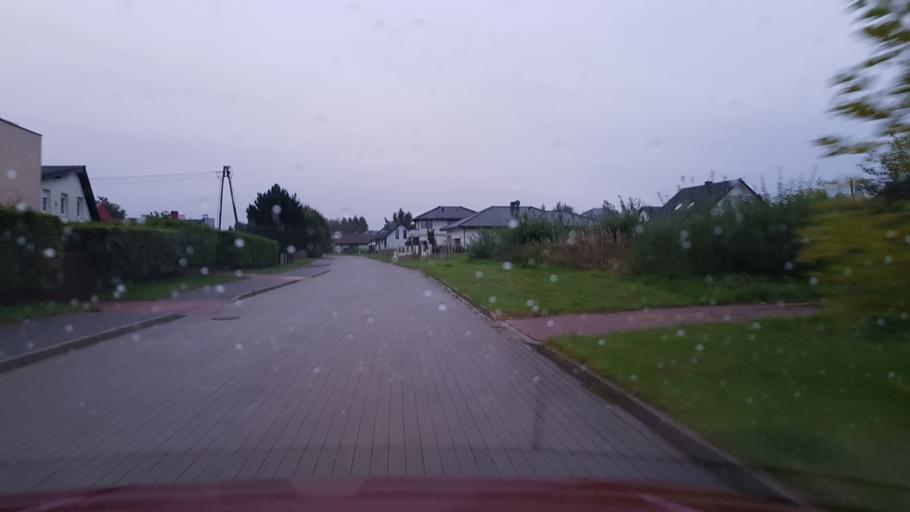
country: PL
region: West Pomeranian Voivodeship
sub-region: Powiat slawienski
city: Slawno
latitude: 54.3461
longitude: 16.6724
